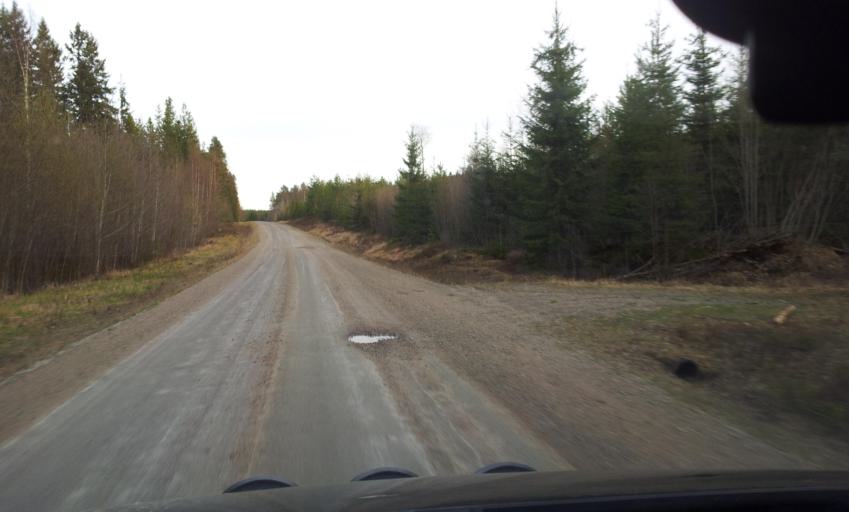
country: SE
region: Gaevleborg
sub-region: Ljusdals Kommun
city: Farila
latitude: 62.0893
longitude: 15.7636
